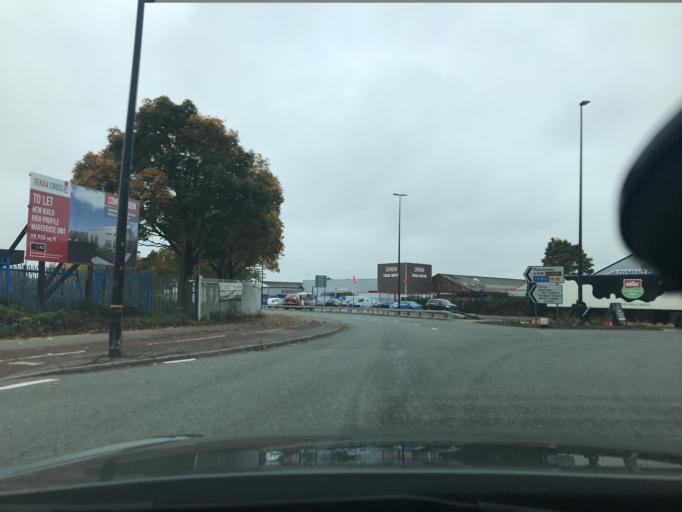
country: GB
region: England
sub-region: Trafford
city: Trafford Park
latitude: 53.4747
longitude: -2.3224
